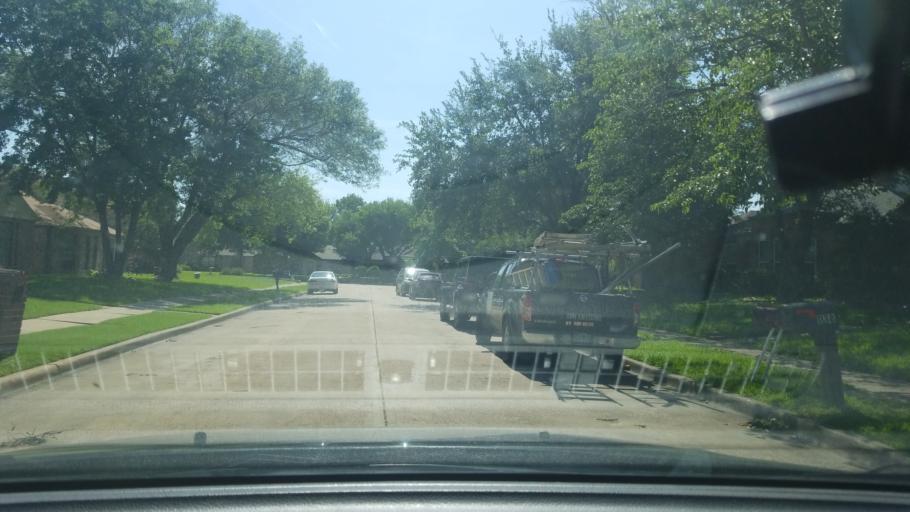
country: US
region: Texas
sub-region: Dallas County
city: Mesquite
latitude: 32.7723
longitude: -96.5822
